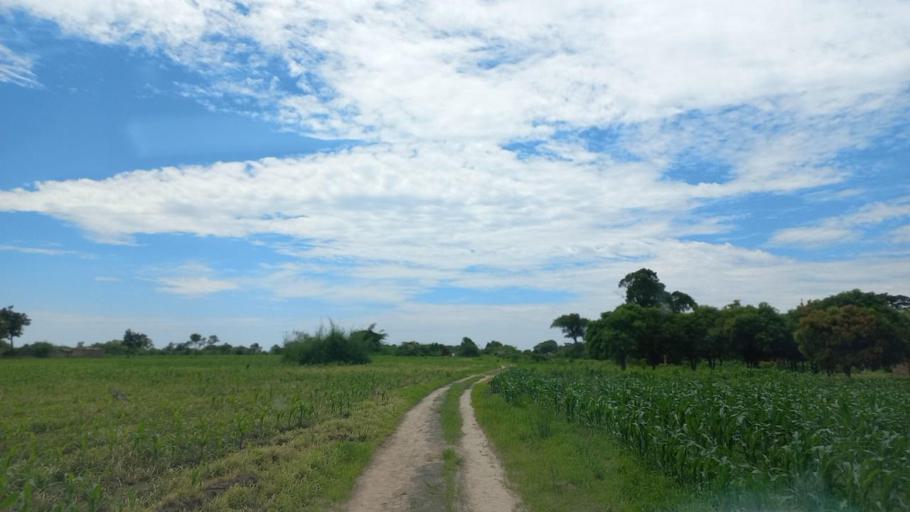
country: ZM
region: Copperbelt
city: Kitwe
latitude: -12.7948
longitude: 28.4013
